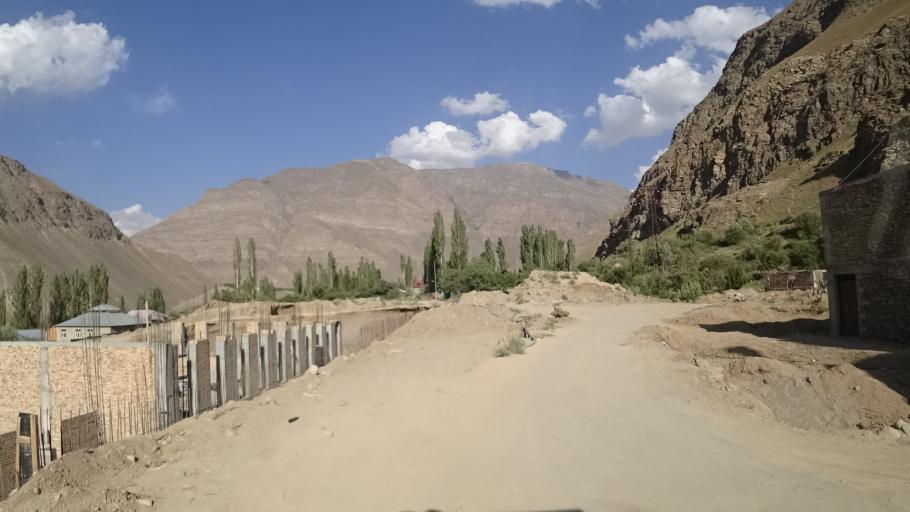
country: TJ
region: Gorno-Badakhshan
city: Khorugh
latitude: 37.4873
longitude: 71.5596
